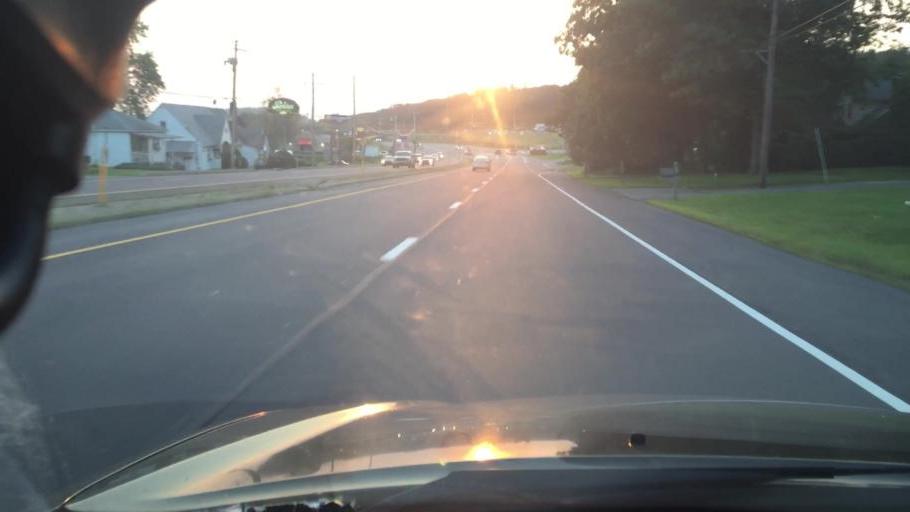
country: US
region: Pennsylvania
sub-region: Luzerne County
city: West Hazleton
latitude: 40.9814
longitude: -76.0209
